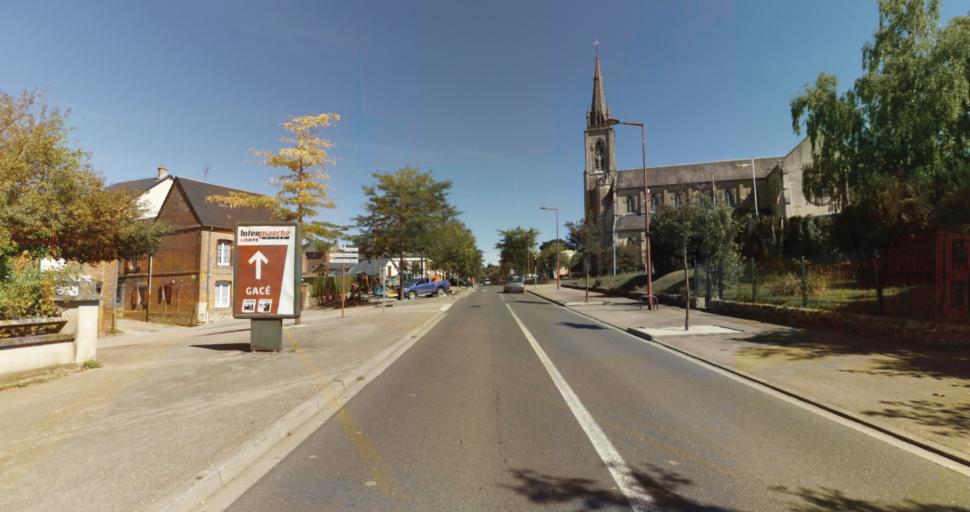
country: FR
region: Lower Normandy
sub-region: Departement de l'Orne
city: Gace
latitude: 48.7934
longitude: 0.2967
